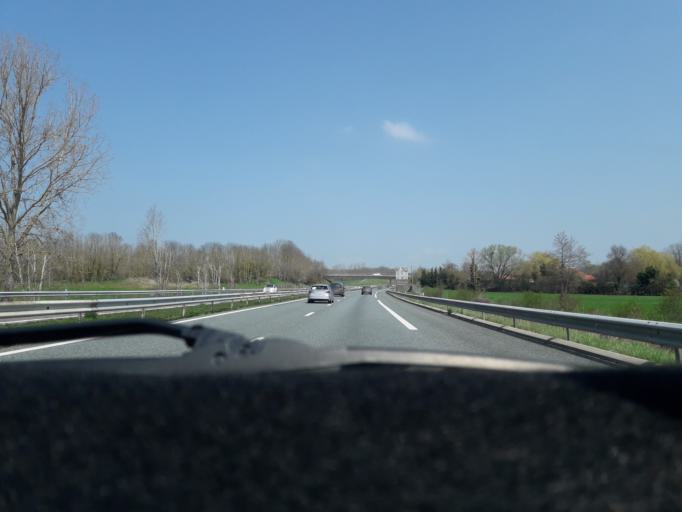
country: FR
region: Rhone-Alpes
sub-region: Departement de l'Isere
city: Saint-Victor-de-Cessieu
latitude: 45.5020
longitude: 5.3998
